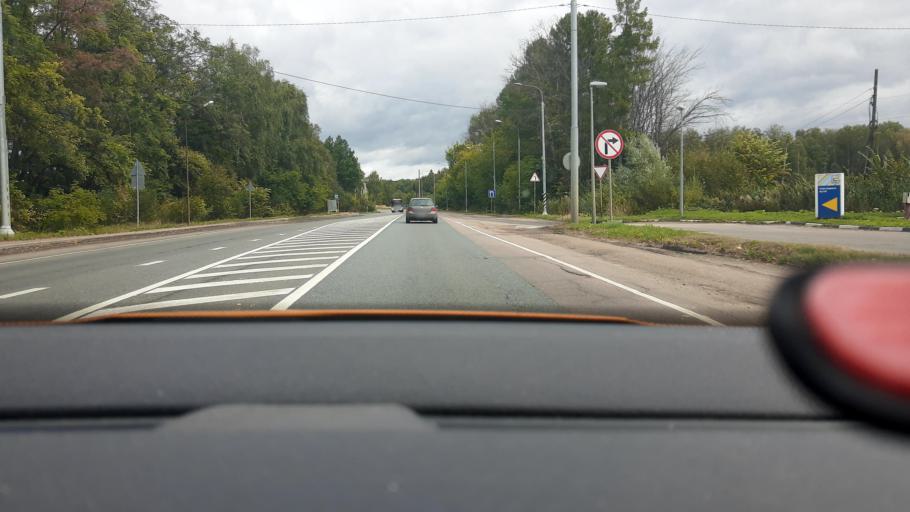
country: RU
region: Moskovskaya
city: Kostino
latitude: 56.0246
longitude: 37.9491
